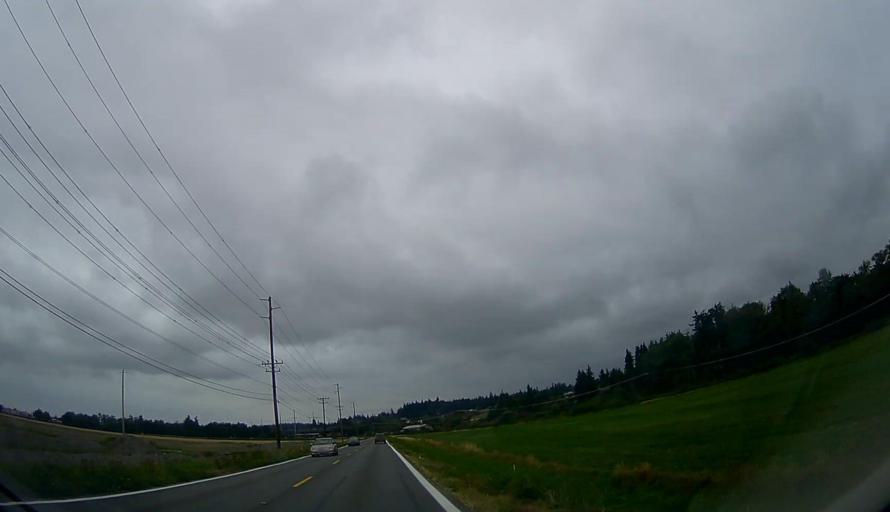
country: US
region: Washington
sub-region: Snohomish County
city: Stanwood
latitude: 48.2343
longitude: -122.3465
